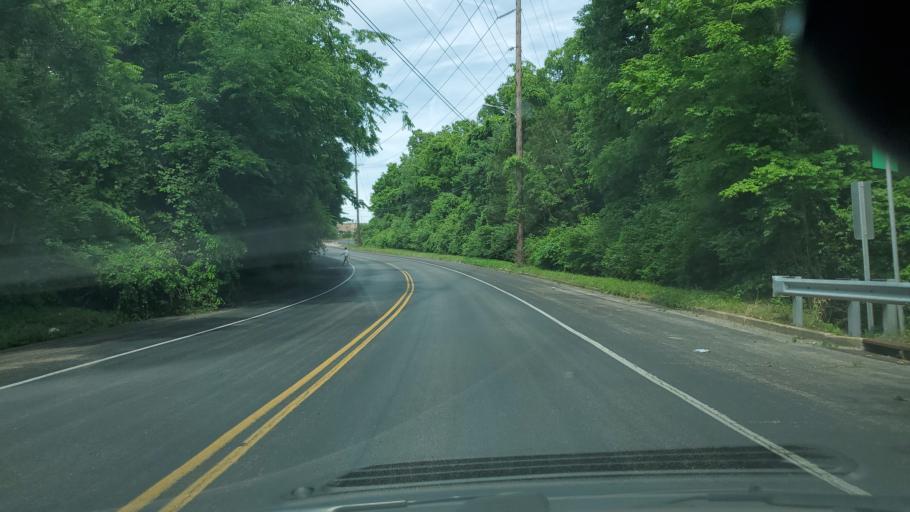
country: US
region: Tennessee
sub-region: Davidson County
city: Oak Hill
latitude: 36.1140
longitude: -86.6991
